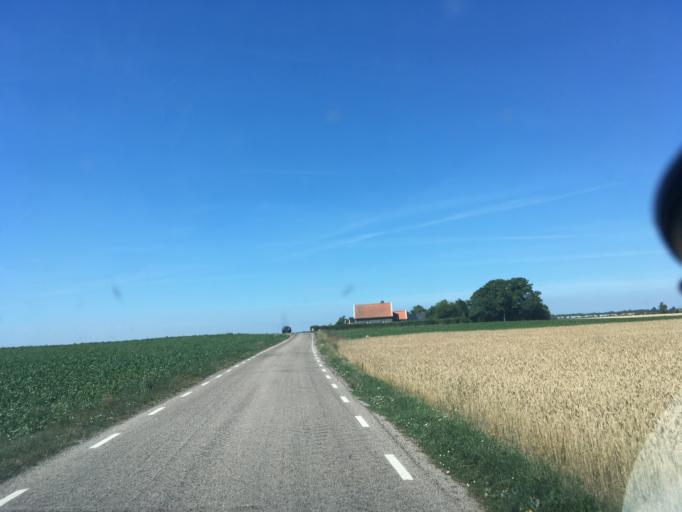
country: SE
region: Skane
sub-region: Trelleborgs Kommun
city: Skare
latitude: 55.3943
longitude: 13.0352
